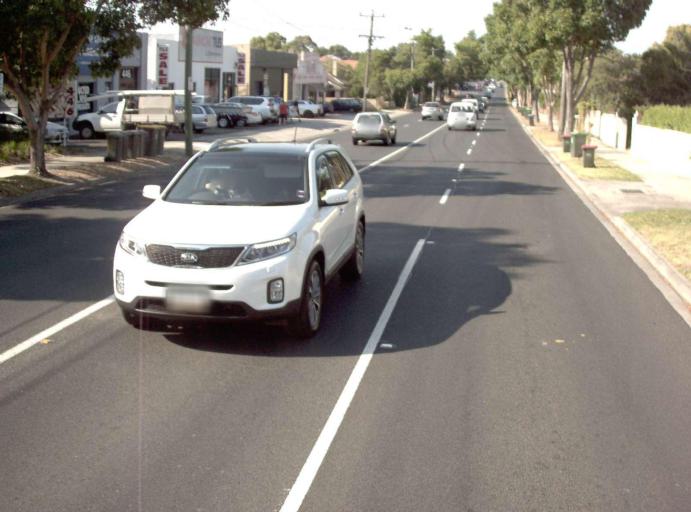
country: AU
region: Victoria
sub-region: Whitehorse
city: Box Hill South
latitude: -37.8257
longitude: 145.1224
